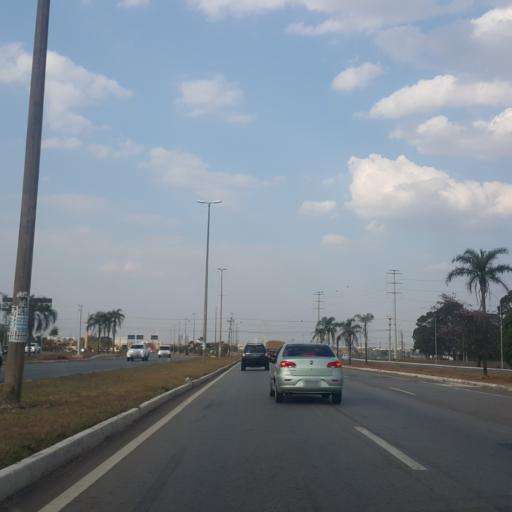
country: BR
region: Federal District
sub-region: Brasilia
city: Brasilia
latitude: -15.8823
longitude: -48.0598
